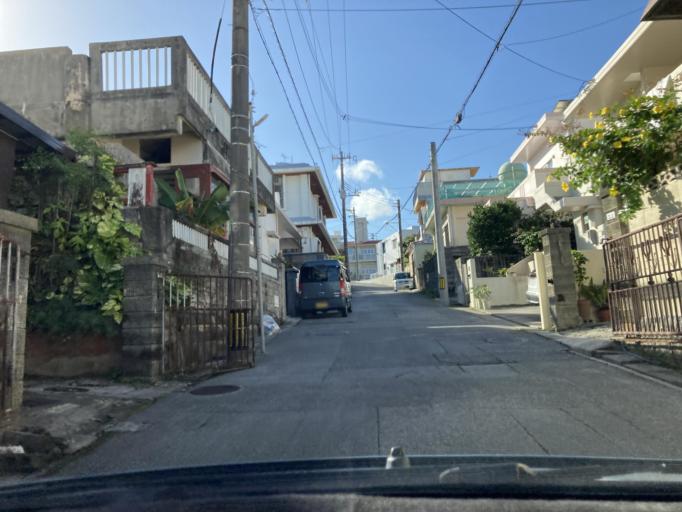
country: JP
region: Okinawa
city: Ginowan
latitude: 26.2388
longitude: 127.7263
